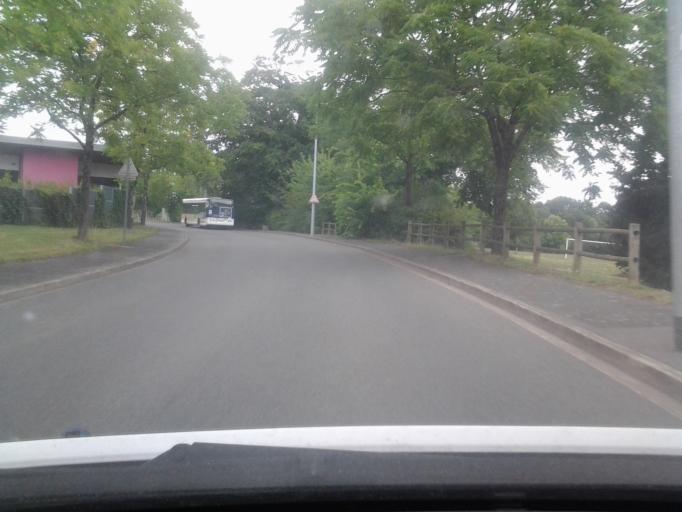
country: FR
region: Pays de la Loire
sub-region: Departement de la Vendee
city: La Roche-sur-Yon
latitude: 46.6557
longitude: -1.4236
